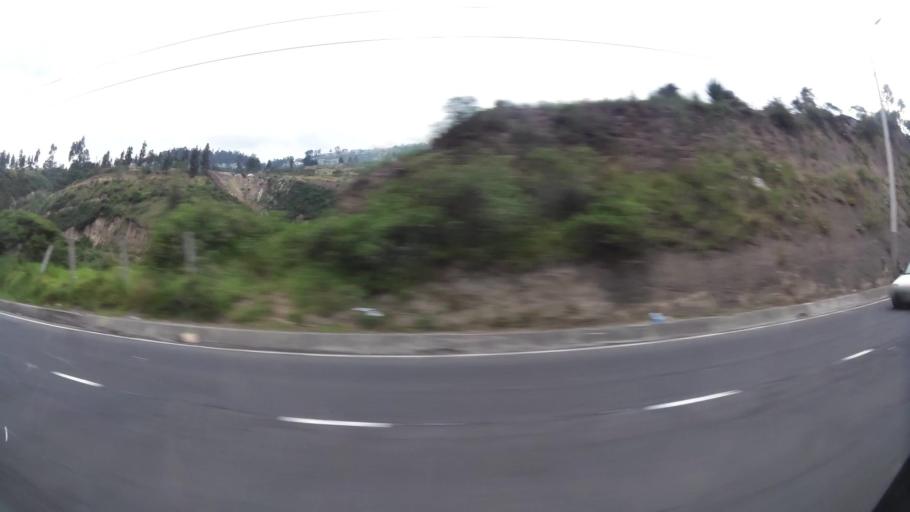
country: EC
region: Pichincha
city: Quito
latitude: -0.1216
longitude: -78.4479
